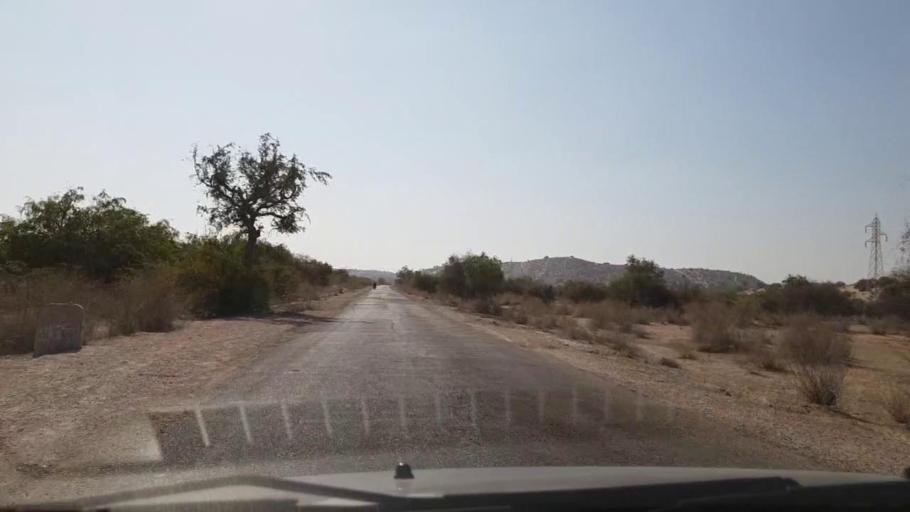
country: PK
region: Sindh
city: Mithi
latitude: 24.6503
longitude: 69.7508
